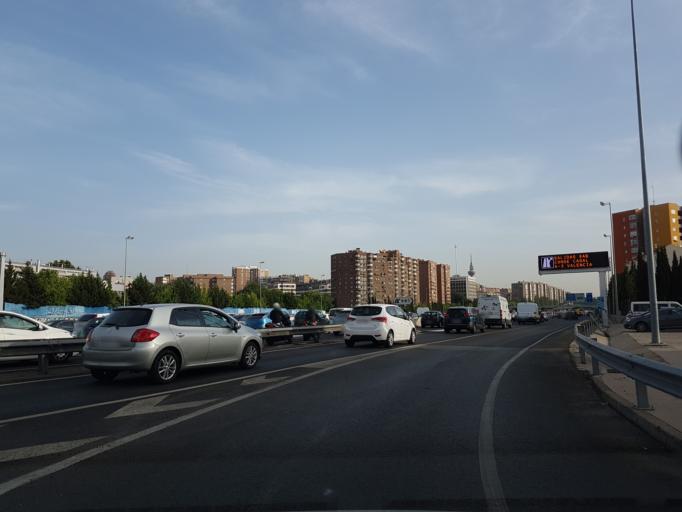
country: ES
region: Madrid
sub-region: Provincia de Madrid
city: Puente de Vallecas
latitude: 40.4011
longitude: -3.6672
